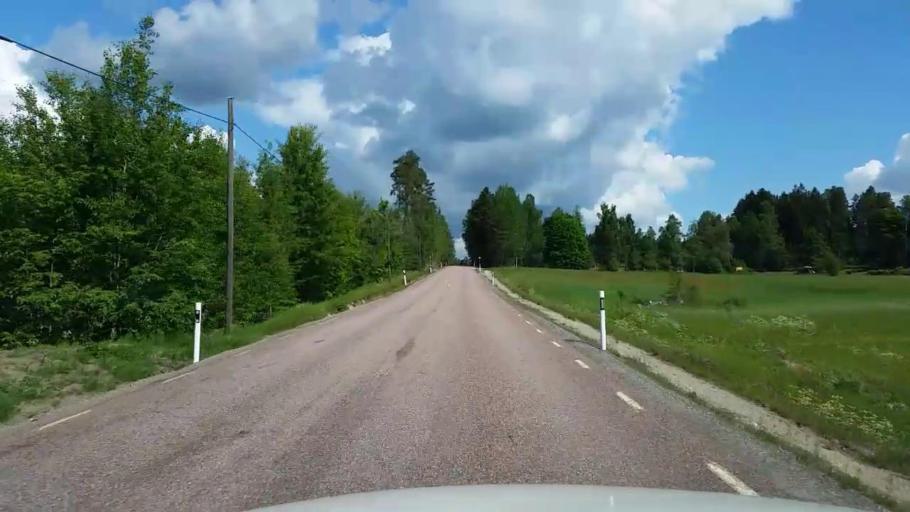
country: SE
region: Vaestmanland
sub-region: Kopings Kommun
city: Kolsva
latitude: 59.6882
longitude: 15.7743
